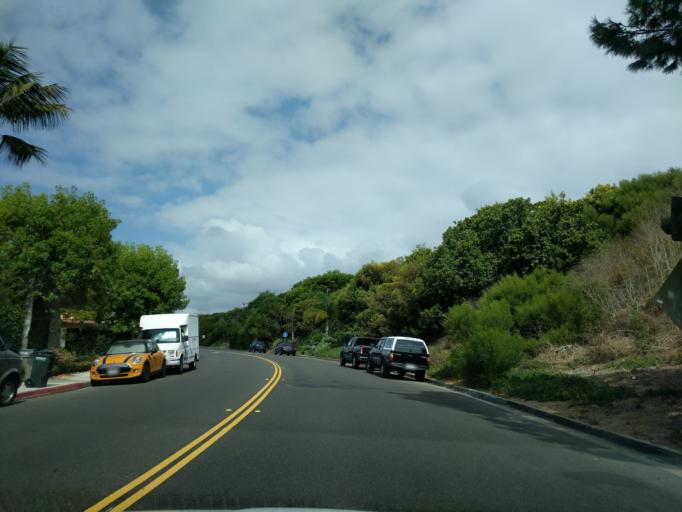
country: US
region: California
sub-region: Orange County
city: San Joaquin Hills
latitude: 33.6021
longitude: -117.8814
